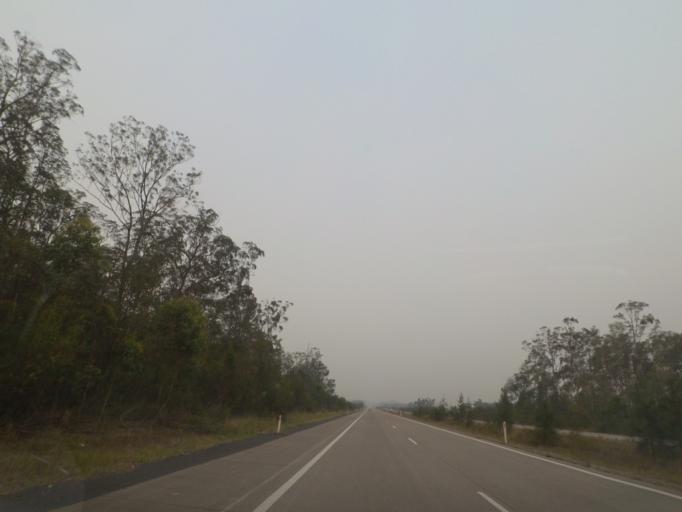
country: AU
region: New South Wales
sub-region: Kempsey
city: Frederickton
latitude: -30.9177
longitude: 152.8942
